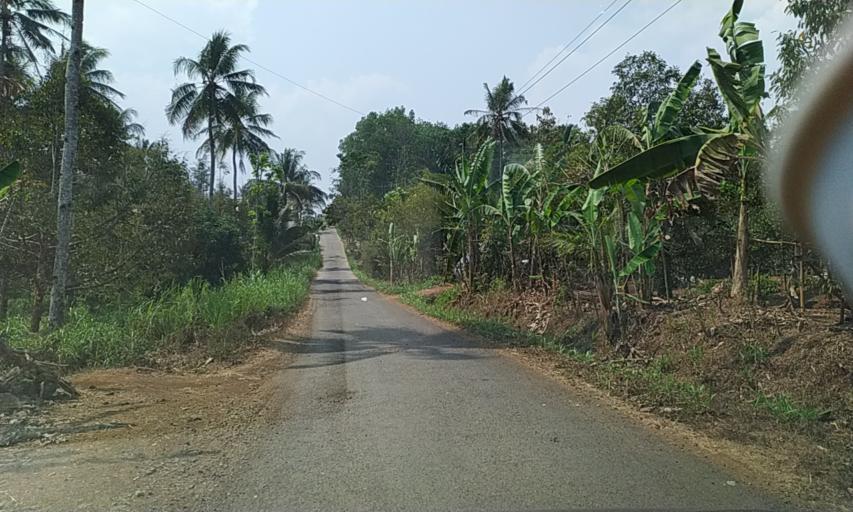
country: ID
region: Central Java
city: Karanggintung
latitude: -7.4476
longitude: 108.8553
